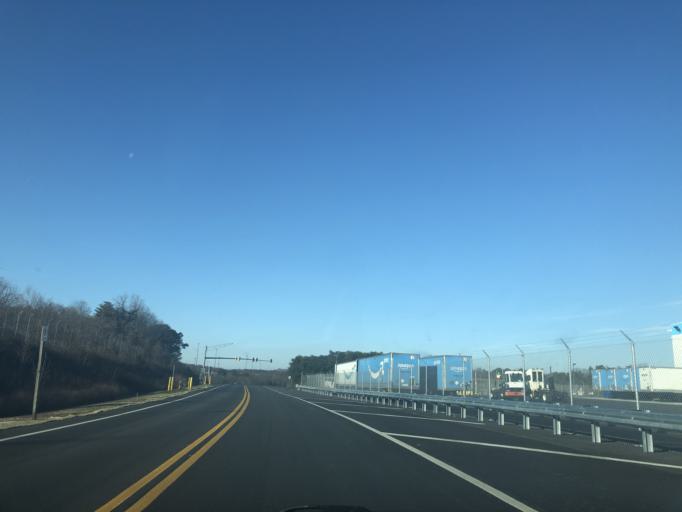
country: US
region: Maryland
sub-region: Anne Arundel County
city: Severn
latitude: 39.1708
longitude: -76.6873
